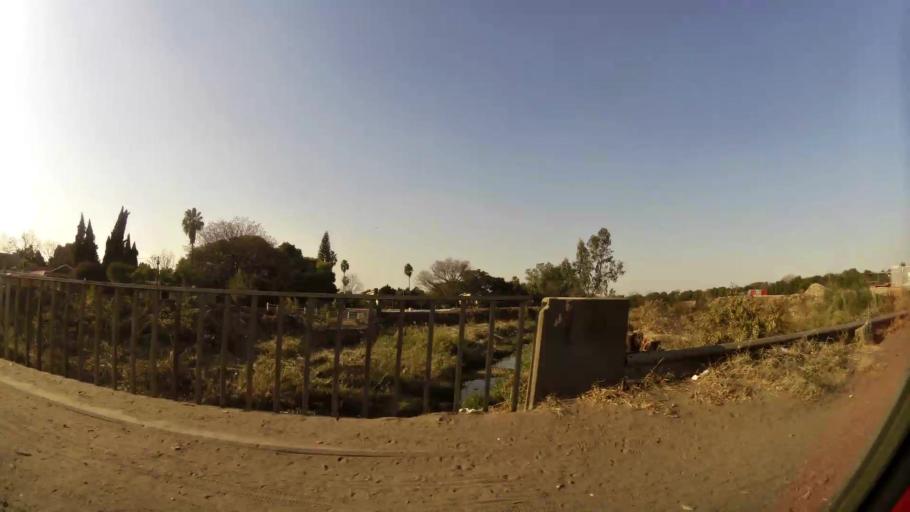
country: ZA
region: North-West
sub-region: Bojanala Platinum District Municipality
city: Rustenburg
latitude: -25.6526
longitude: 27.2417
